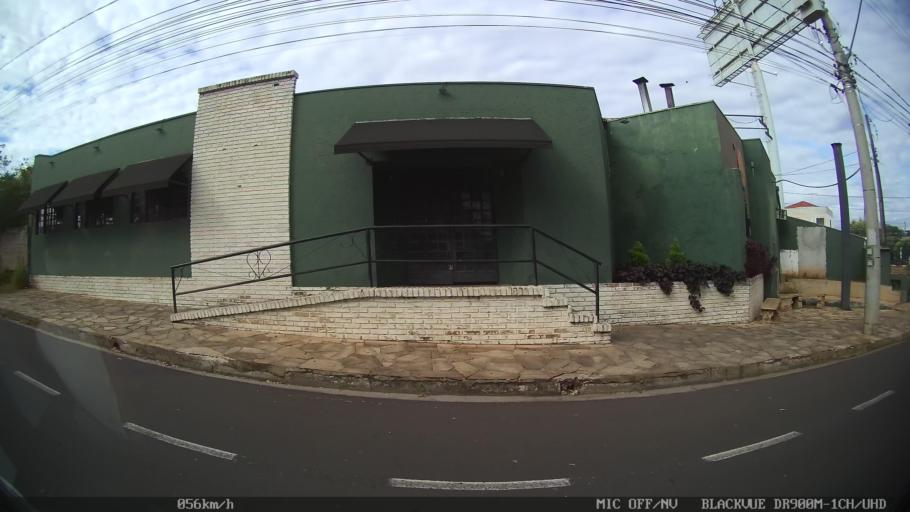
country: BR
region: Sao Paulo
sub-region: Sao Jose Do Rio Preto
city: Sao Jose do Rio Preto
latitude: -20.8242
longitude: -49.3978
